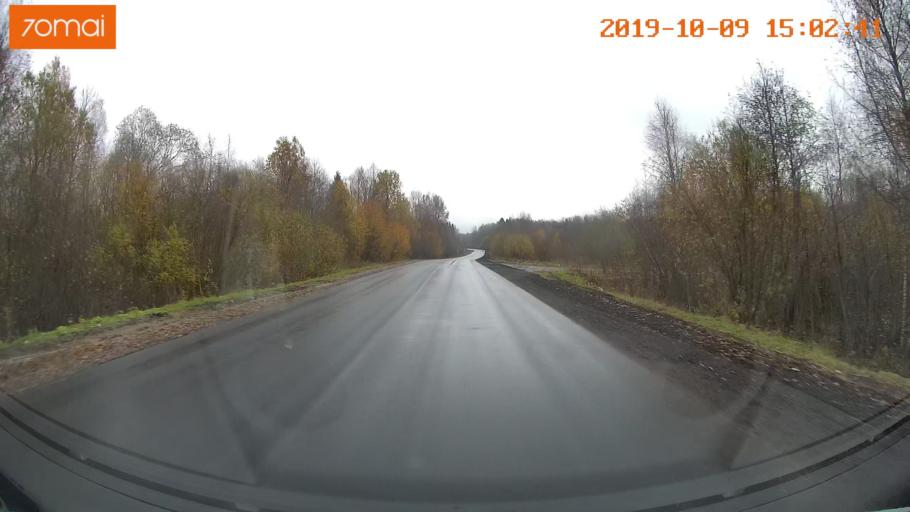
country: RU
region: Kostroma
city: Chistyye Bory
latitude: 58.2816
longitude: 41.6778
